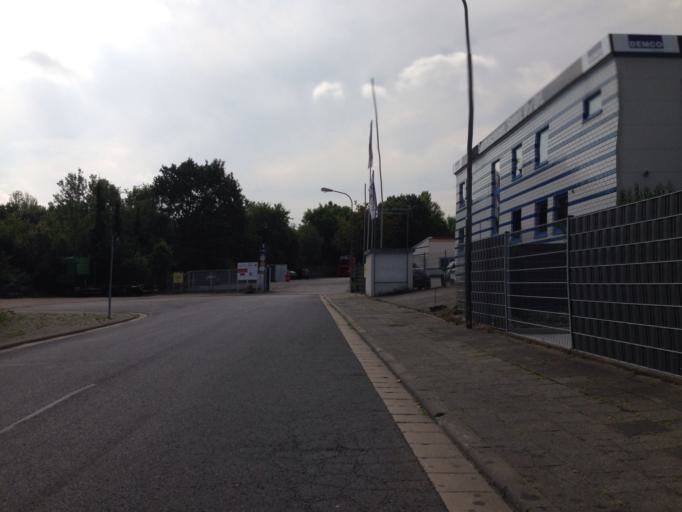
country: DE
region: Hesse
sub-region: Regierungsbezirk Giessen
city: Giessen
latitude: 50.5951
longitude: 8.7100
